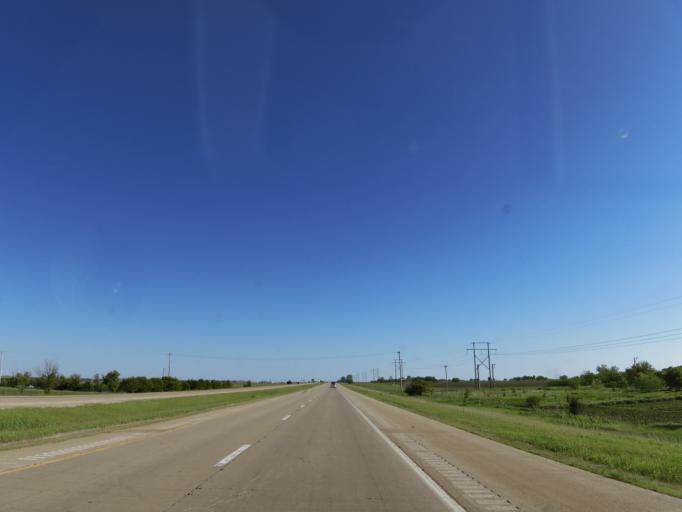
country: US
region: Illinois
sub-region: Woodford County
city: Minonk
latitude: 40.9419
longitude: -89.0568
